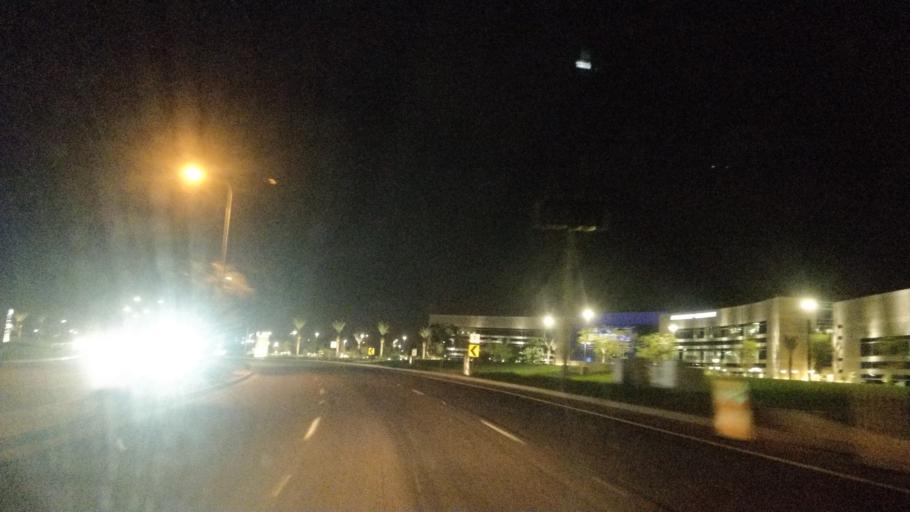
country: US
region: Arizona
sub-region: Maricopa County
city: Chandler
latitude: 33.2801
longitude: -111.8895
